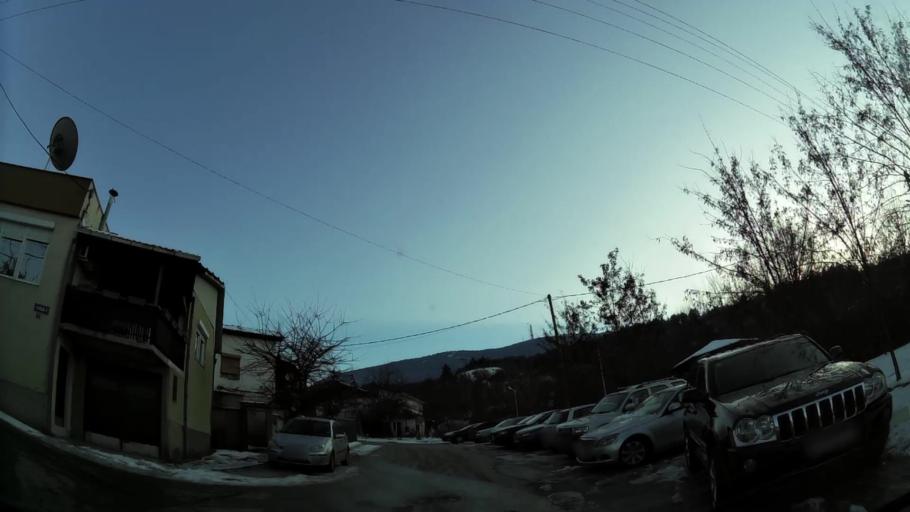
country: MK
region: Karpos
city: Skopje
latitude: 41.9894
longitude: 21.4059
